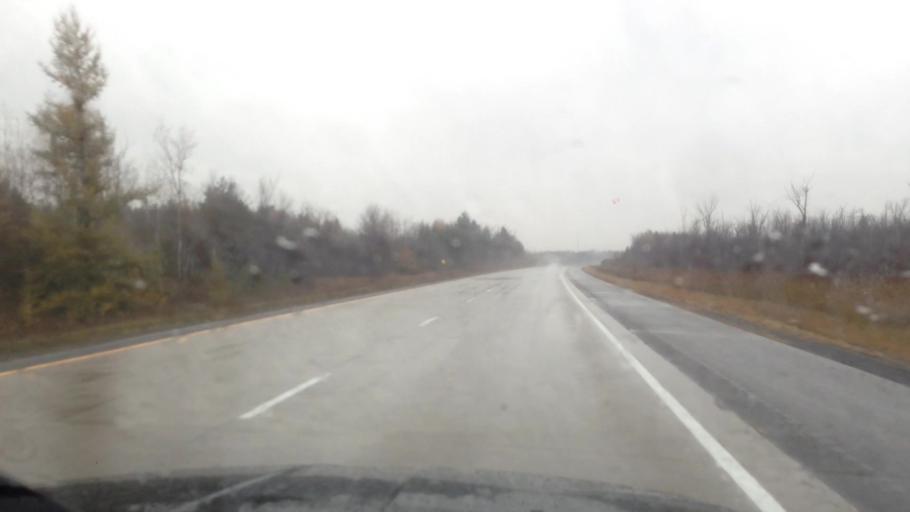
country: CA
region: Ontario
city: Hawkesbury
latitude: 45.4887
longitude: -74.6269
